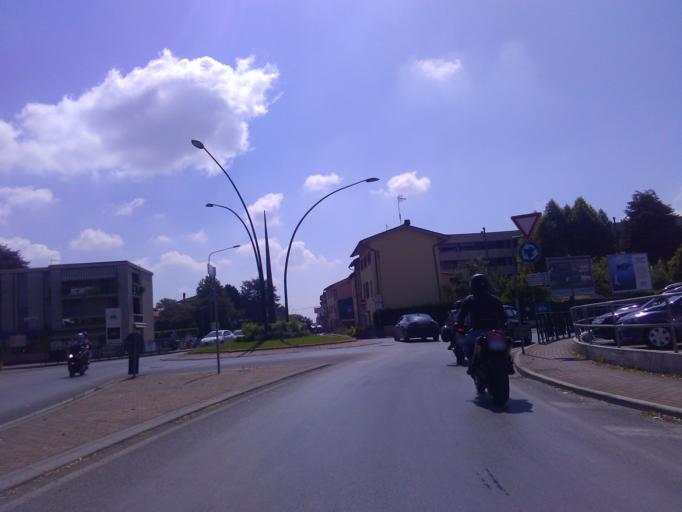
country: IT
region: Tuscany
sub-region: Provincia di Lucca
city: Lucca
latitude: 43.8471
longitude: 10.4730
